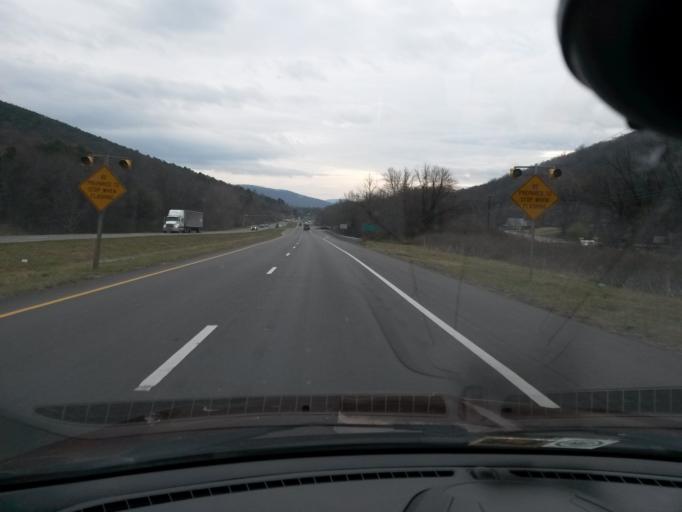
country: US
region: Virginia
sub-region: Botetourt County
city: Cloverdale
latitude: 37.3551
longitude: -79.8848
